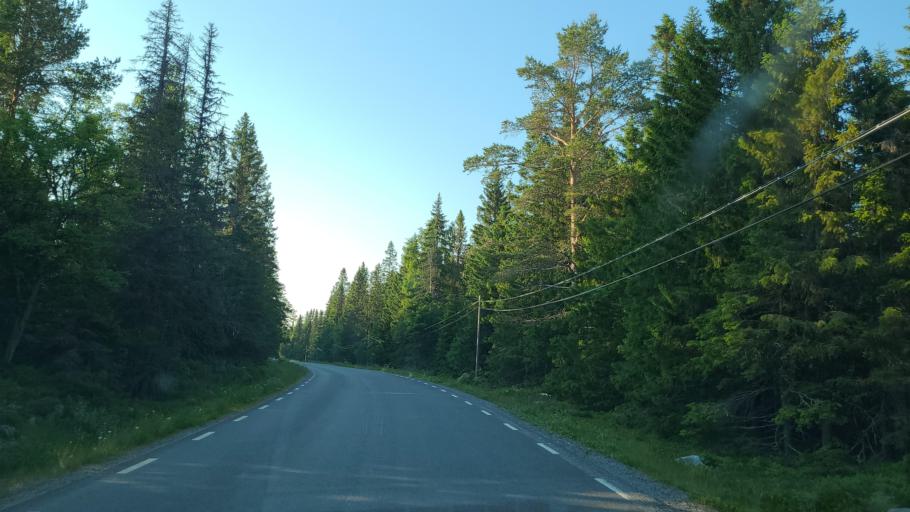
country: SE
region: Vaesterbotten
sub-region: Skelleftea Kommun
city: Burea
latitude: 64.4635
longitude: 21.5871
